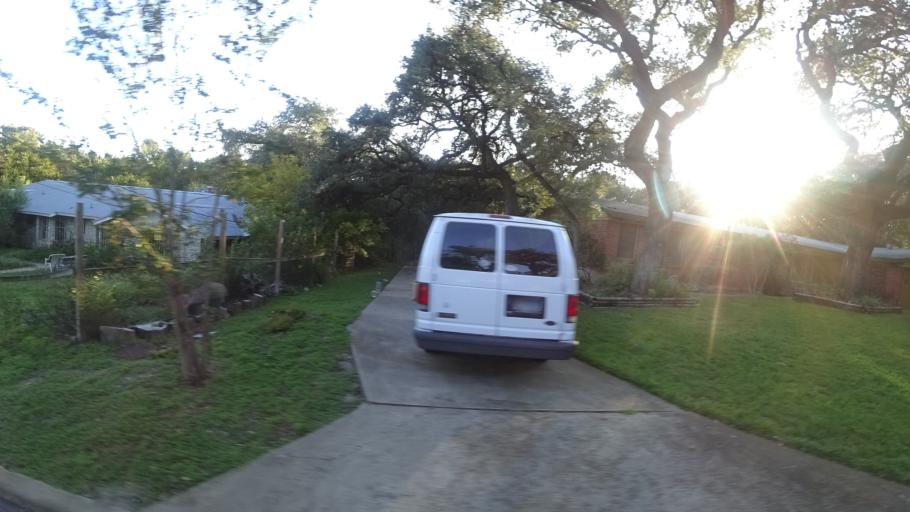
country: US
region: Texas
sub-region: Travis County
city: Wells Branch
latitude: 30.3630
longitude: -97.6733
